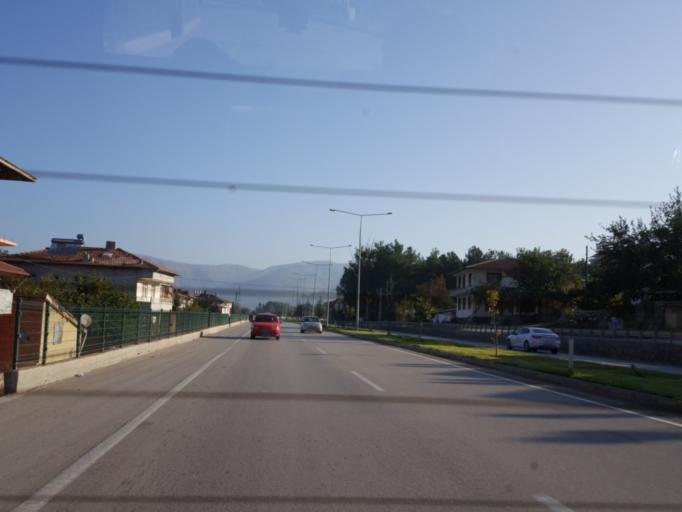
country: TR
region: Amasya
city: Amasya
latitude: 40.5836
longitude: 35.7930
